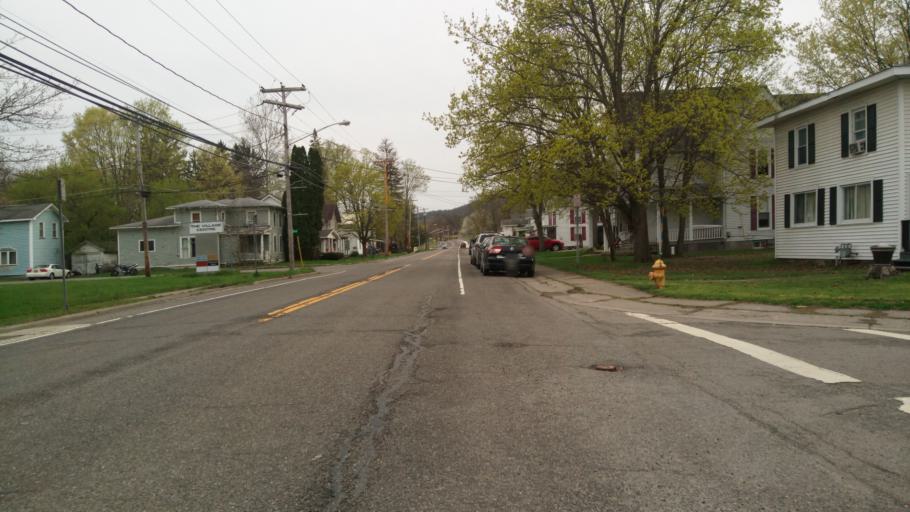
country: US
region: New York
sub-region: Chemung County
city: Southport
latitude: 42.0127
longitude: -76.7283
